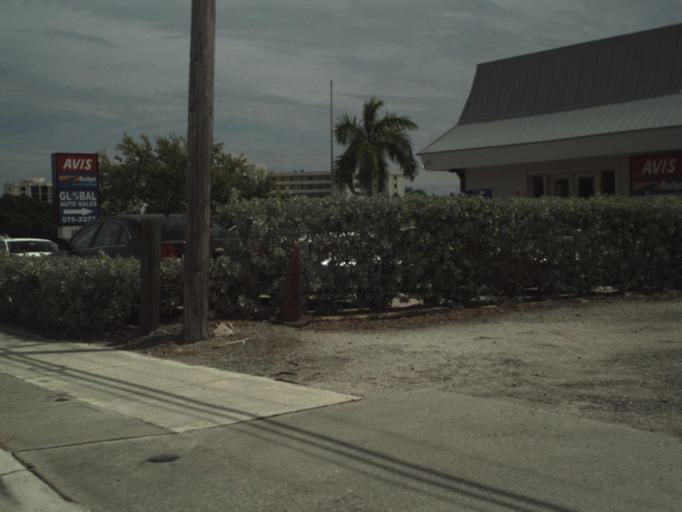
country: US
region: Florida
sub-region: Palm Beach County
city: Jupiter
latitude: 26.9645
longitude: -80.0852
